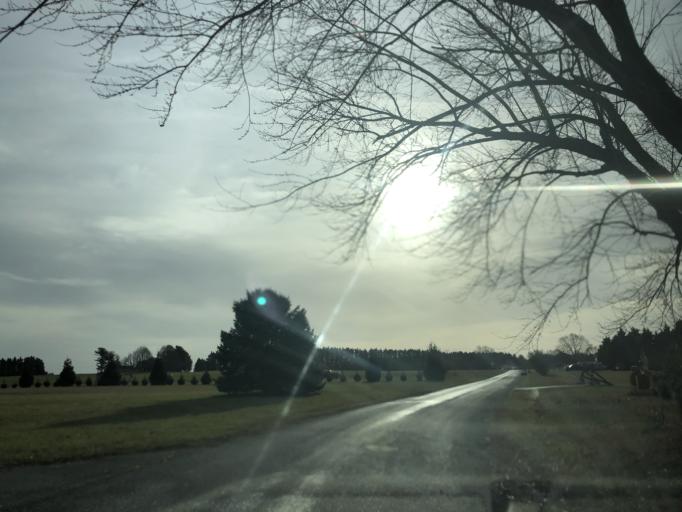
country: US
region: Delaware
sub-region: New Castle County
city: Townsend
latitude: 39.4526
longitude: -75.6330
